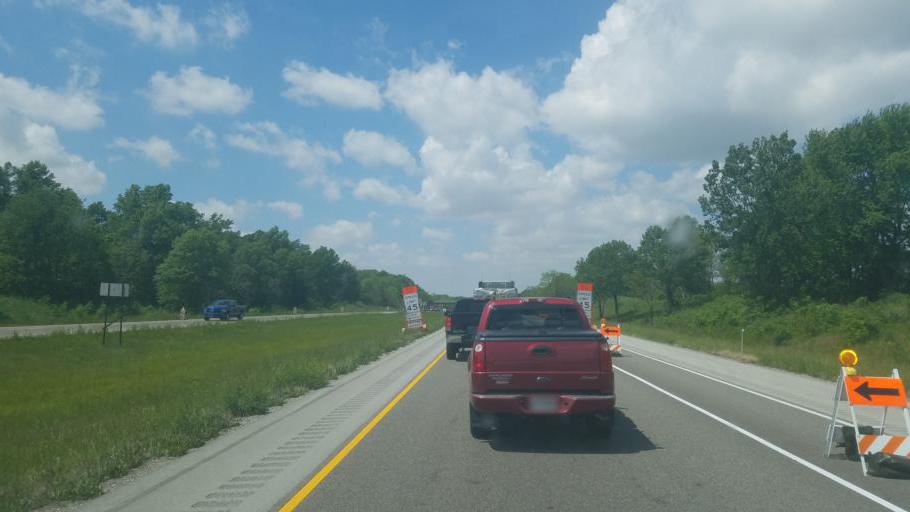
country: US
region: Illinois
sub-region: Cumberland County
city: Toledo
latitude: 39.2210
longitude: -88.2391
